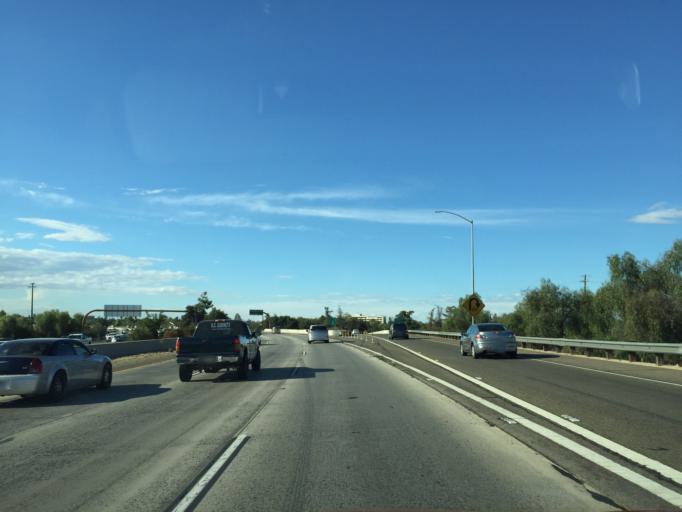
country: US
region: California
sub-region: Fresno County
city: Fresno
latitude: 36.7633
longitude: -119.7756
